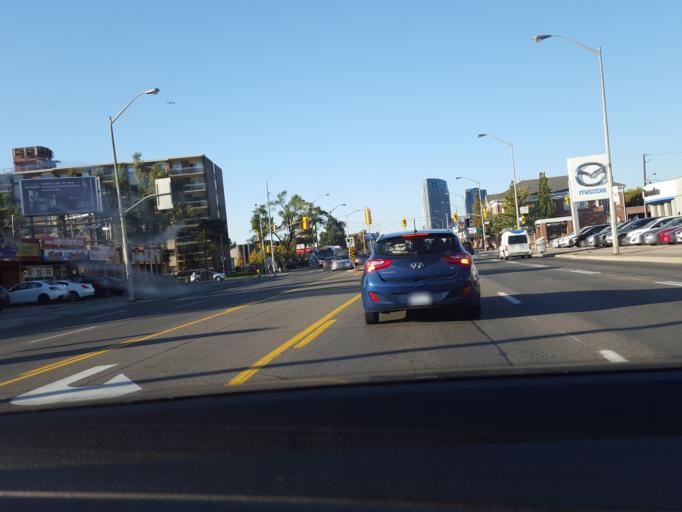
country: CA
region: Ontario
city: North York
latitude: 43.7930
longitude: -79.4188
